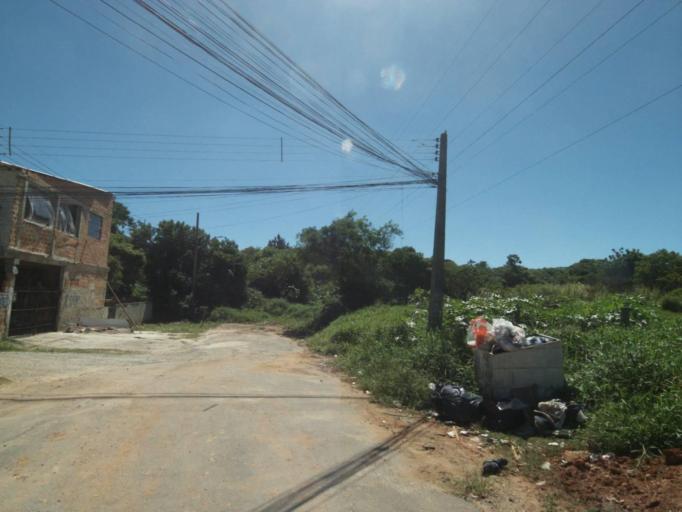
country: BR
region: Parana
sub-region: Curitiba
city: Curitiba
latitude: -25.4738
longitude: -49.3357
